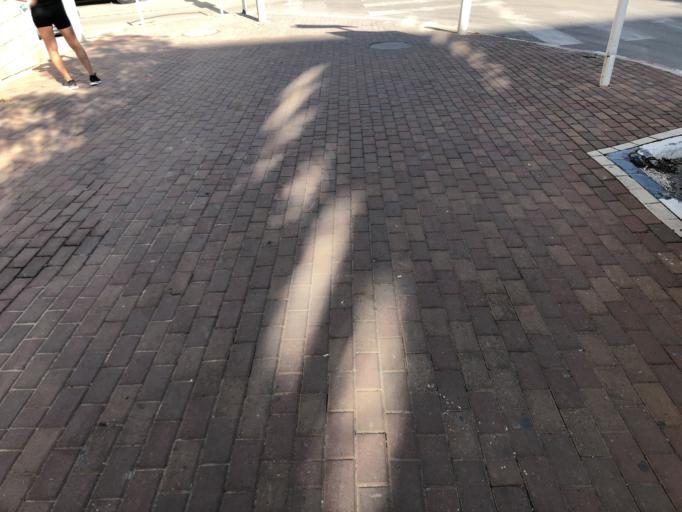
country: IL
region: Tel Aviv
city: Giv`atayim
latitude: 32.0707
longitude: 34.8125
